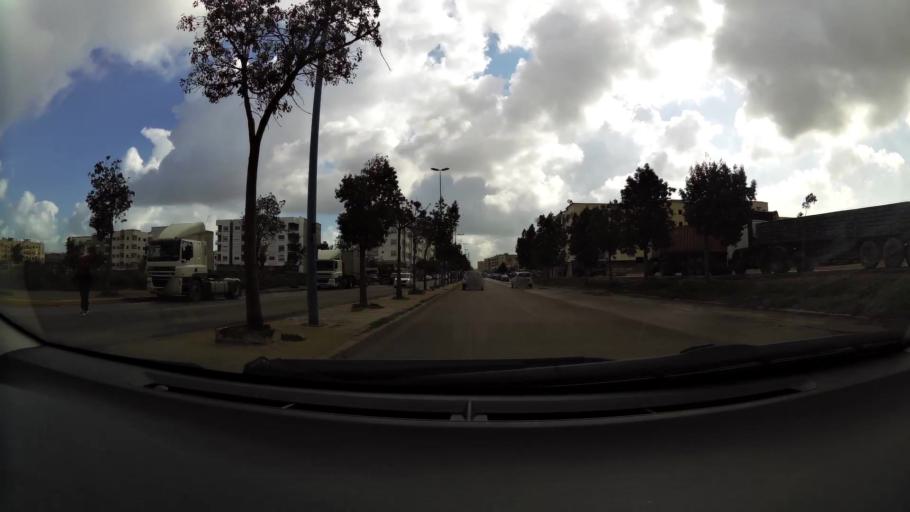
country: MA
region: Grand Casablanca
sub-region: Mediouna
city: Tit Mellil
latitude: 33.5888
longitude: -7.5216
